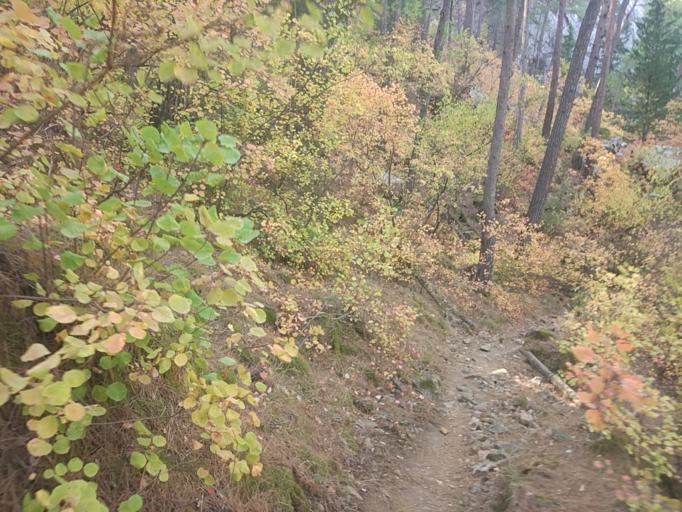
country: TR
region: Antalya
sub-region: Kemer
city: Goeynuek
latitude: 36.6781
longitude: 30.4920
